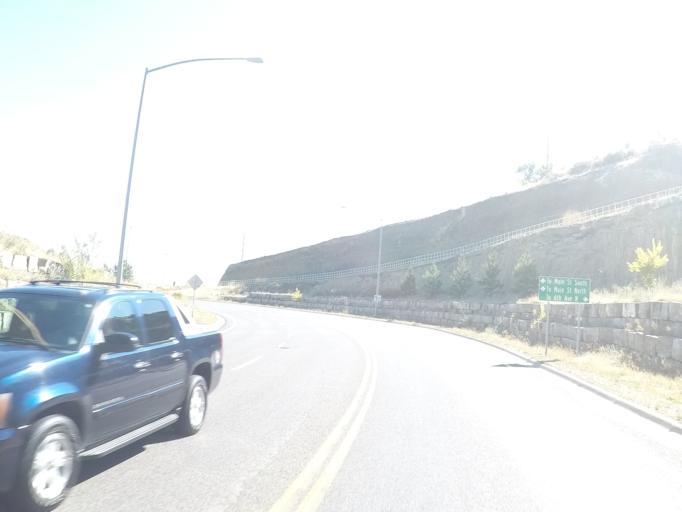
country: US
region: Montana
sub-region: Yellowstone County
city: Billings
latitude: 45.8032
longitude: -108.4835
